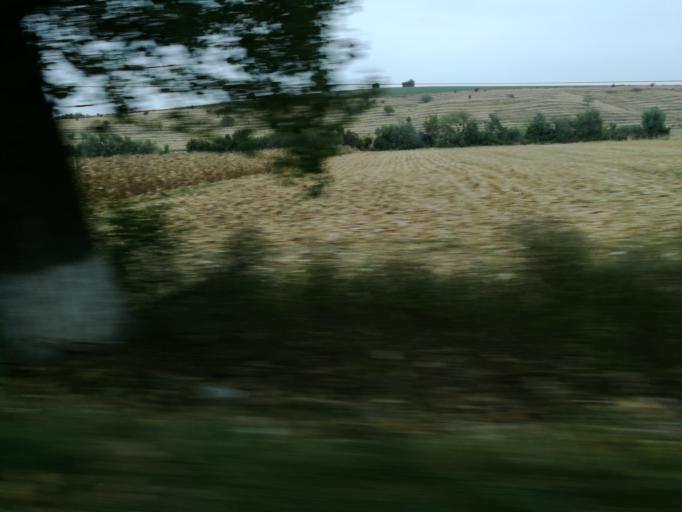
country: RO
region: Tulcea
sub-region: Comuna Ciucurova
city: Ciucurova
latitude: 44.9216
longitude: 28.4563
